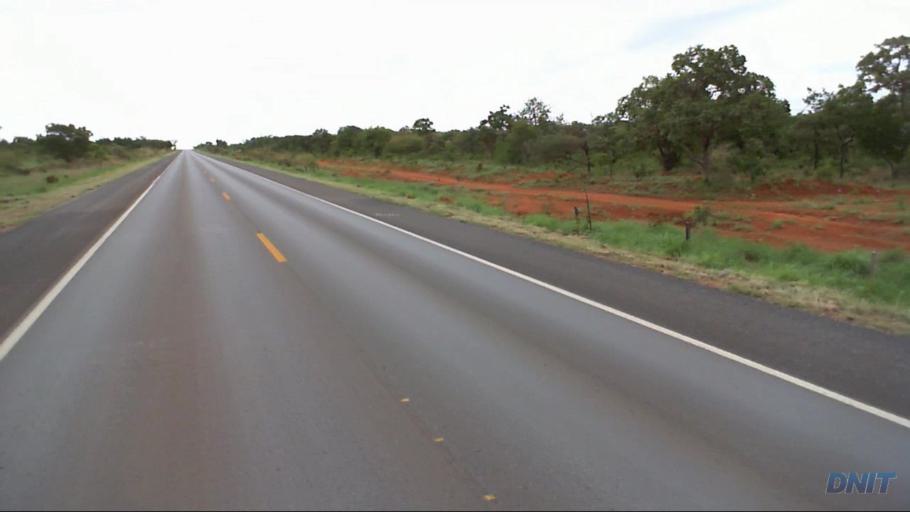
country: BR
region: Goias
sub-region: Barro Alto
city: Barro Alto
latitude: -15.2093
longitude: -48.6776
